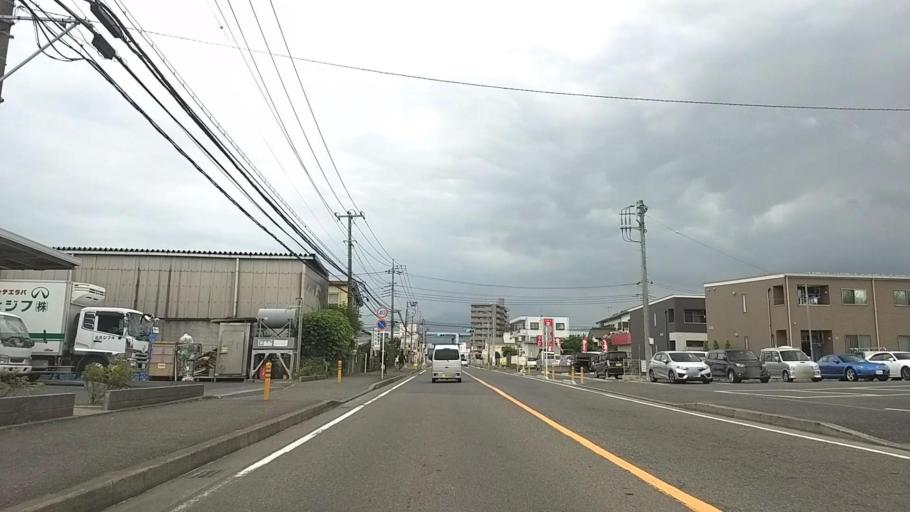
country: JP
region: Kanagawa
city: Chigasaki
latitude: 35.3708
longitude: 139.3794
